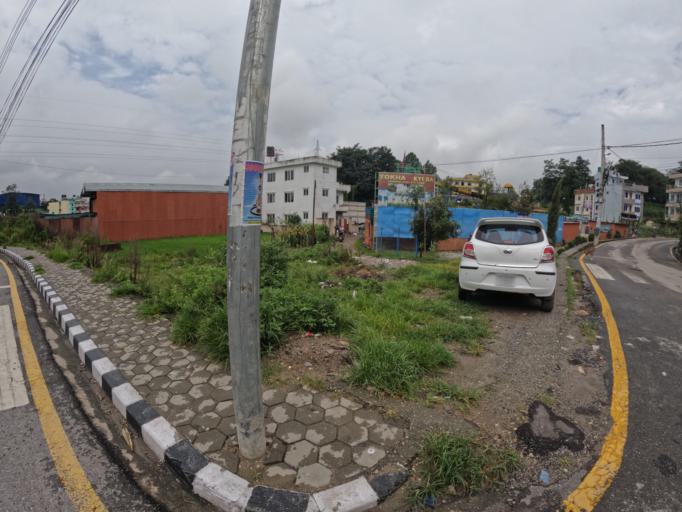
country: NP
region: Central Region
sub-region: Bagmati Zone
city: Kathmandu
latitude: 27.7625
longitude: 85.3289
